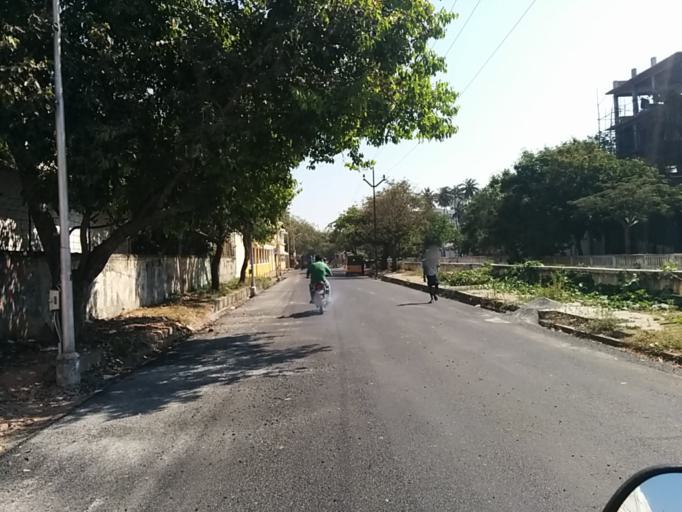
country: IN
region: Pondicherry
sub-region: Puducherry
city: Puducherry
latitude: 11.9315
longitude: 79.8322
